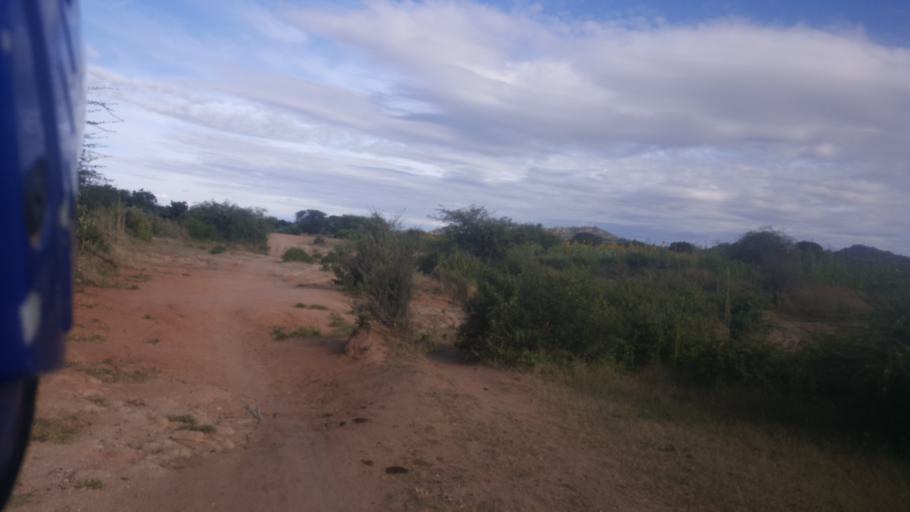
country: TZ
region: Dodoma
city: Dodoma
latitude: -6.0975
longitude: 35.5313
